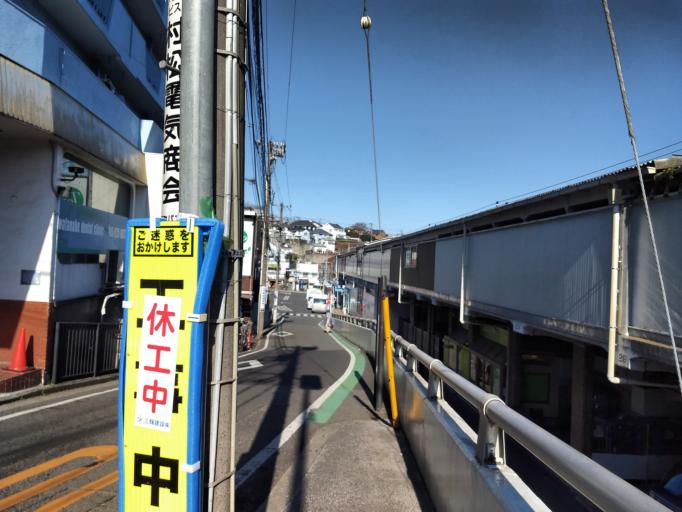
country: JP
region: Kanagawa
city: Yokohama
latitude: 35.4266
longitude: 139.6464
